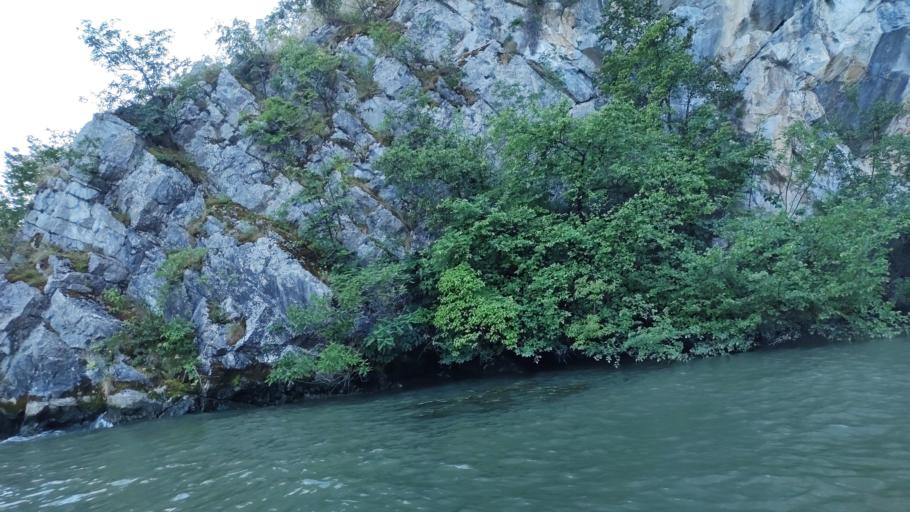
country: RO
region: Mehedinti
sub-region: Comuna Dubova
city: Dubova
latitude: 44.5953
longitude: 22.2614
